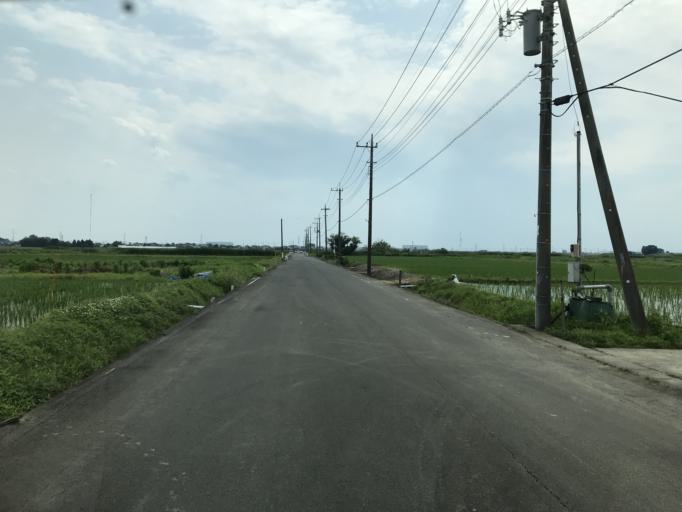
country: JP
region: Saitama
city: Kazo
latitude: 36.0942
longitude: 139.6304
